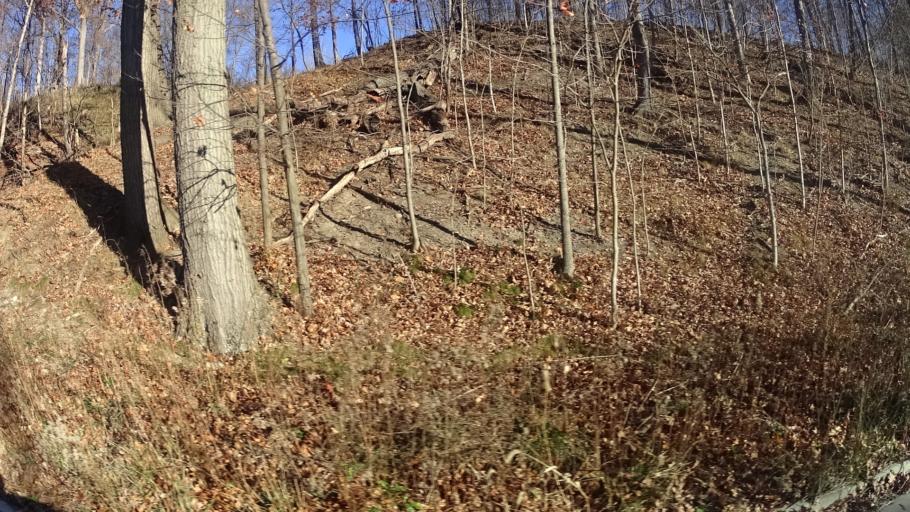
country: US
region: Ohio
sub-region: Lorain County
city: Sheffield
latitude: 41.4123
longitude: -82.0970
